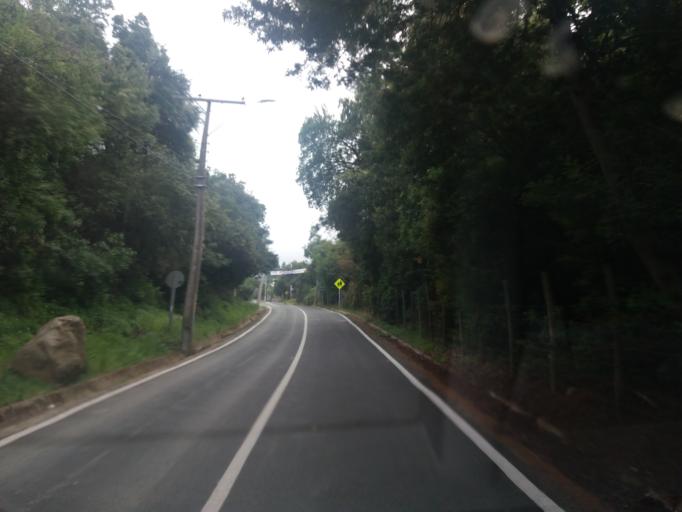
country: CL
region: Valparaiso
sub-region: Provincia de Marga Marga
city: Limache
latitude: -33.0243
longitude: -71.0740
